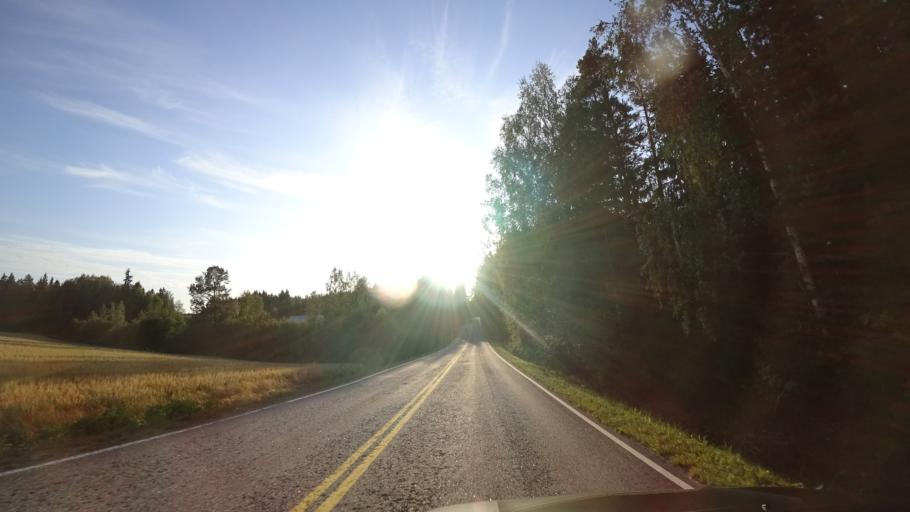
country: FI
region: Haeme
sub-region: Haemeenlinna
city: Tuulos
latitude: 61.0066
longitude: 24.8716
